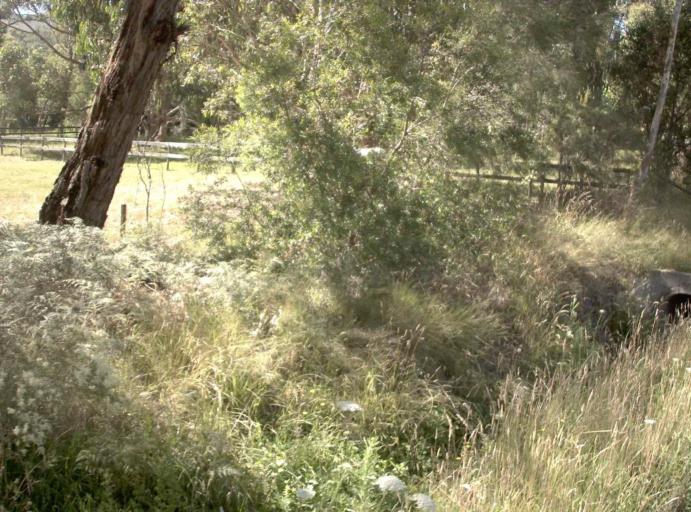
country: AU
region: Victoria
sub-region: Yarra Ranges
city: Badger Creek
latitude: -37.6859
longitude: 145.5452
